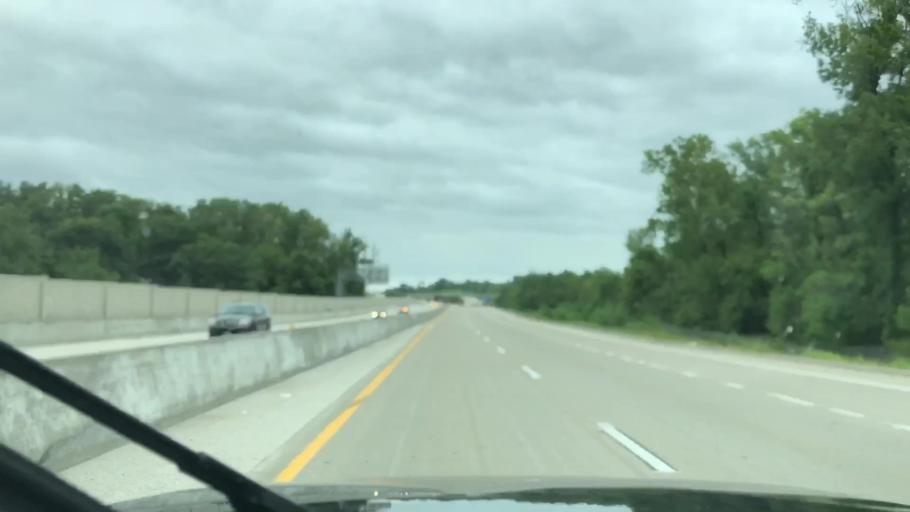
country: US
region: Missouri
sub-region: Saint Louis County
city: Town and Country
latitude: 38.6731
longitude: -90.4938
